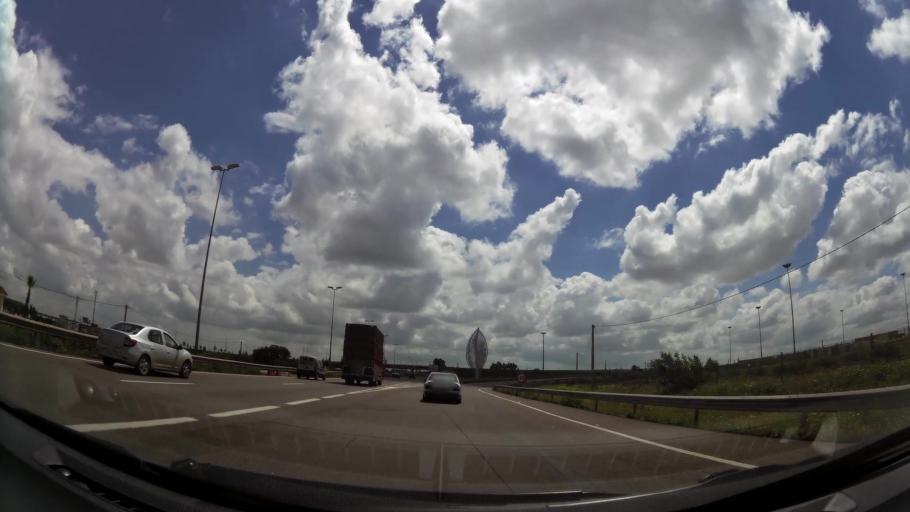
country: MA
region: Chaouia-Ouardigha
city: Nouaseur
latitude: 33.3927
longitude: -7.6204
